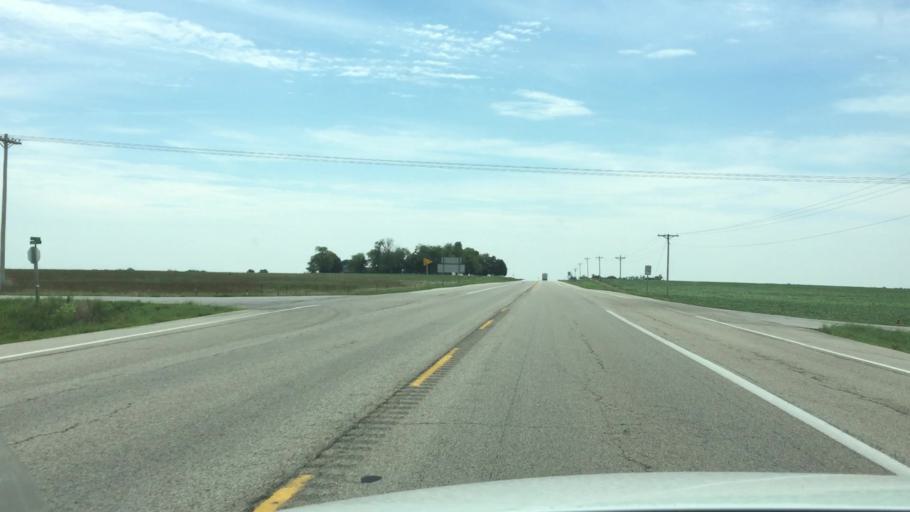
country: US
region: Kansas
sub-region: Nemaha County
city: Sabetha
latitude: 39.7546
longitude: -95.7297
